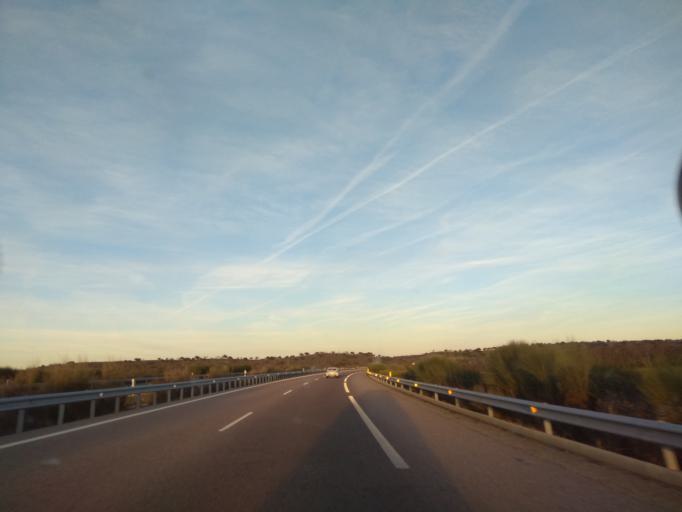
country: ES
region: Castille and Leon
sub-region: Provincia de Salamanca
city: Castraz
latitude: 40.7443
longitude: -6.3493
